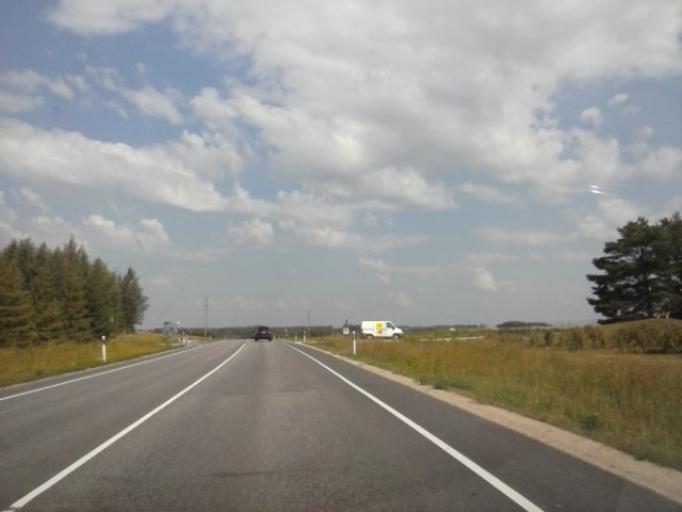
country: EE
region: Tartu
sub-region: Tartu linn
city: Tartu
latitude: 58.4767
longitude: 26.6830
